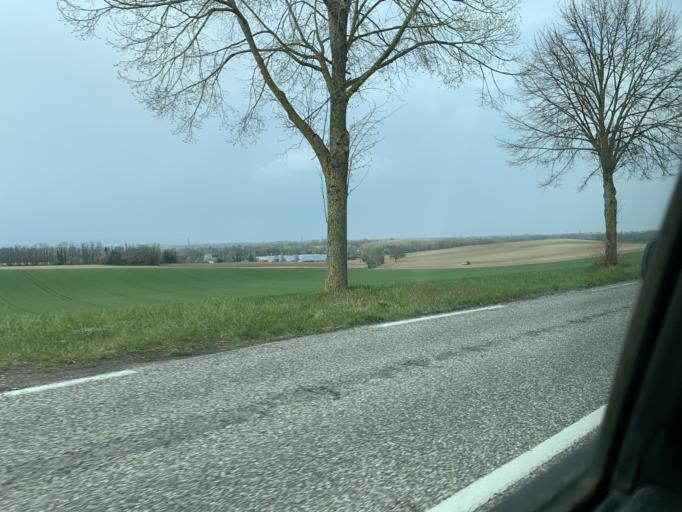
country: FR
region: Alsace
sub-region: Departement du Haut-Rhin
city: Heimsbrunn
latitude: 47.7312
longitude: 7.2332
